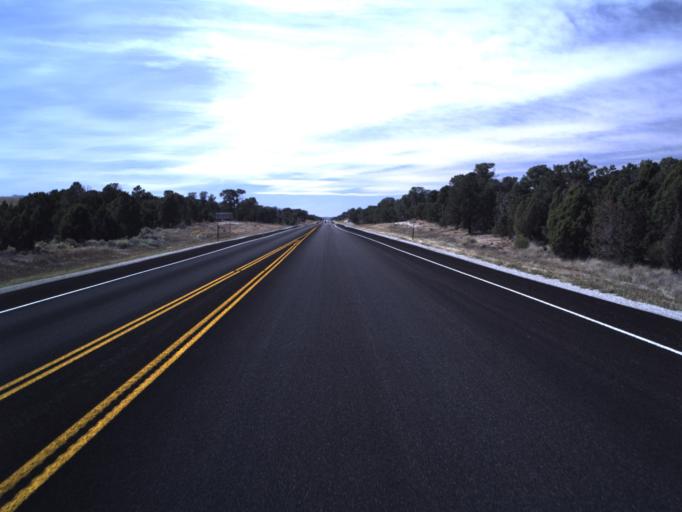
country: US
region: Colorado
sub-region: Dolores County
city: Dove Creek
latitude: 37.8236
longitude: -109.0668
